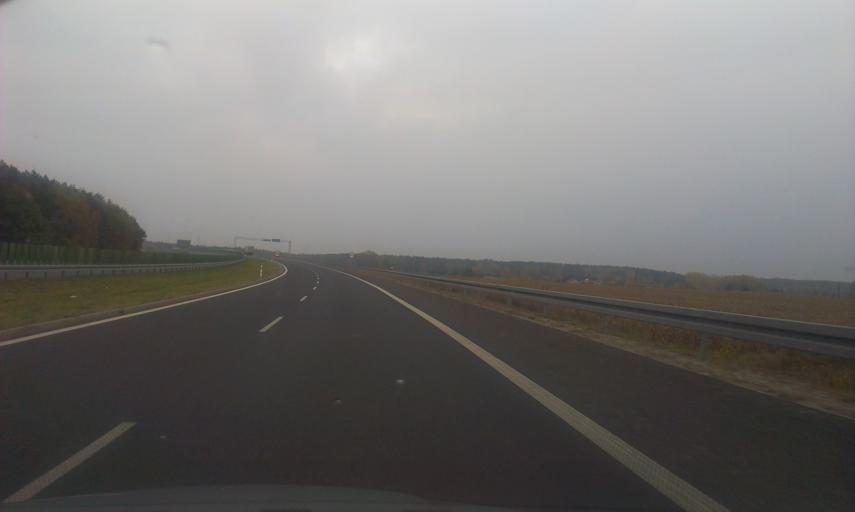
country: PL
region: Greater Poland Voivodeship
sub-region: Powiat poznanski
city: Zlotniki
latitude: 52.5145
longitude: 16.8255
